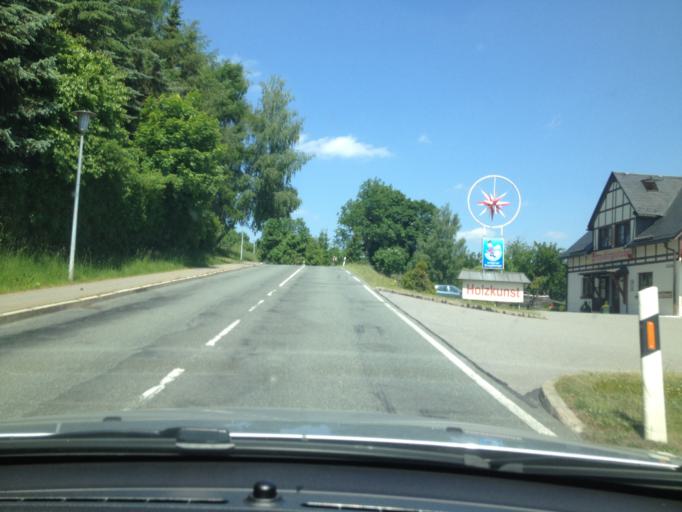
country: DE
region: Saxony
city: Wiesa
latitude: 50.6150
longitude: 12.9854
